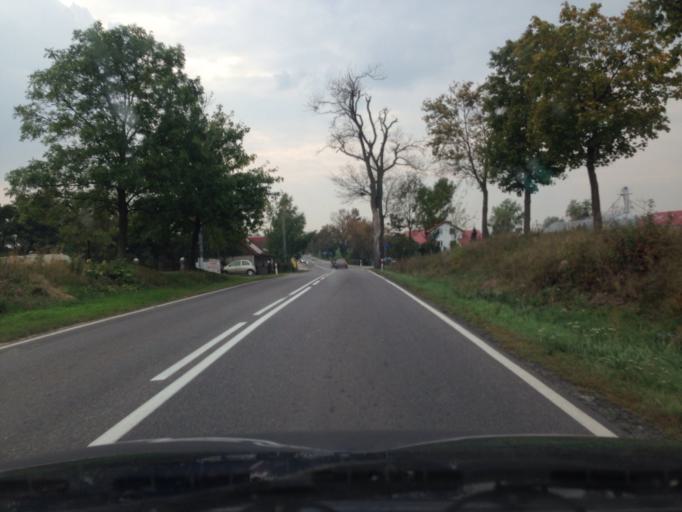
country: PL
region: Pomeranian Voivodeship
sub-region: Powiat kwidzynski
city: Kwidzyn
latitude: 53.7748
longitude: 18.9532
